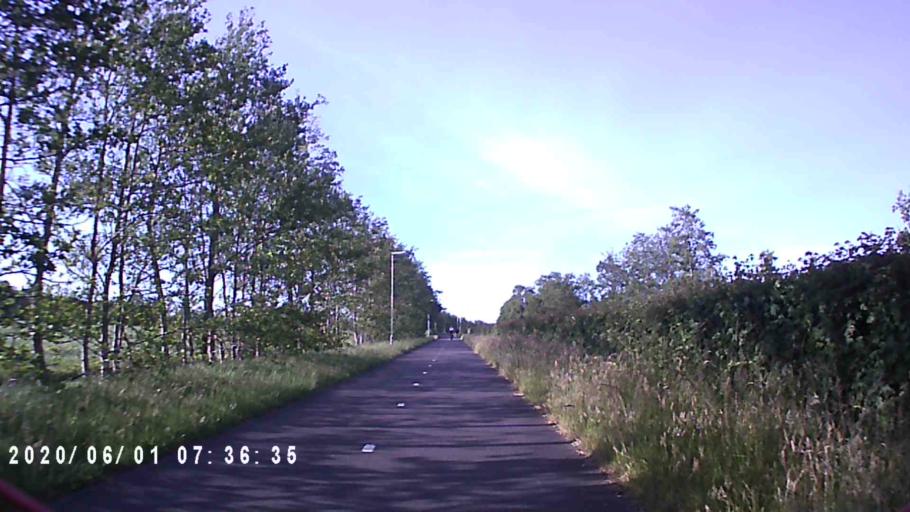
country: NL
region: Friesland
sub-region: Gemeente Dantumadiel
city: Damwald
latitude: 53.3026
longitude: 5.9950
